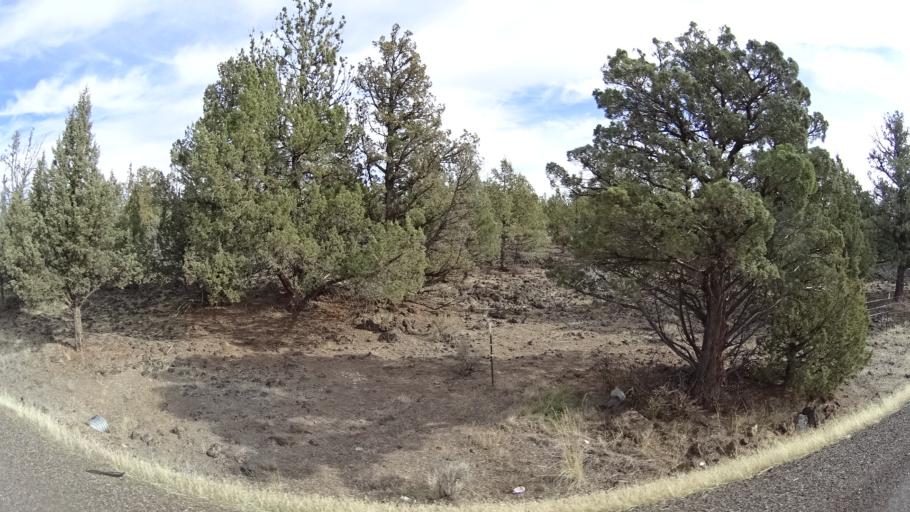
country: US
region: California
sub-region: Siskiyou County
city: Weed
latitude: 41.6003
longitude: -122.3953
